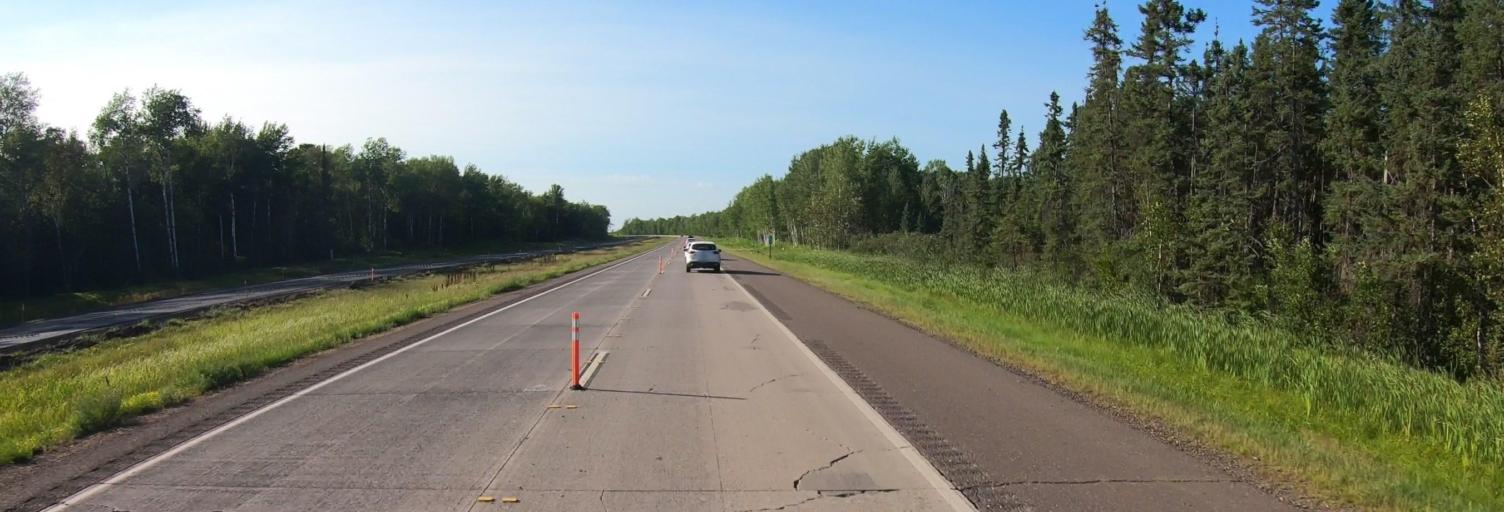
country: US
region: Minnesota
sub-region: Saint Louis County
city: Hermantown
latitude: 46.8841
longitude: -92.3528
